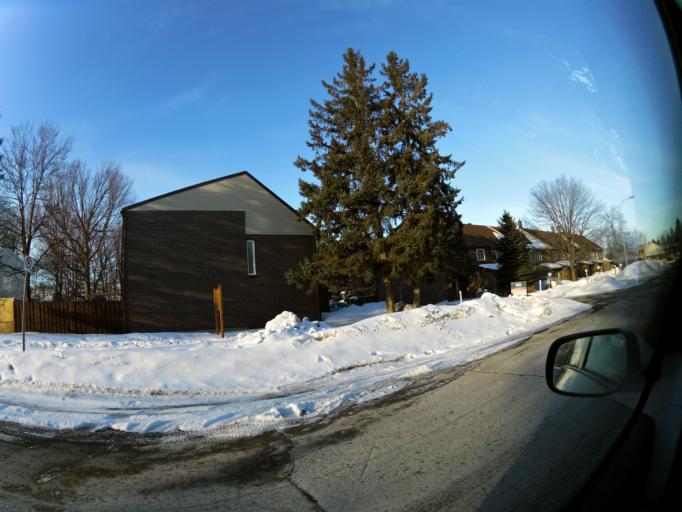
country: CA
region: Ontario
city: Ottawa
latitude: 45.4283
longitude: -75.5670
